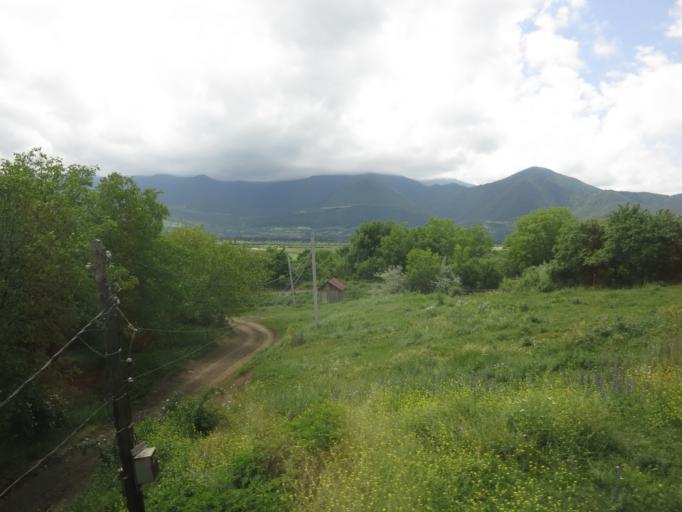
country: GE
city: Surami
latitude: 41.9898
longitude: 43.5483
